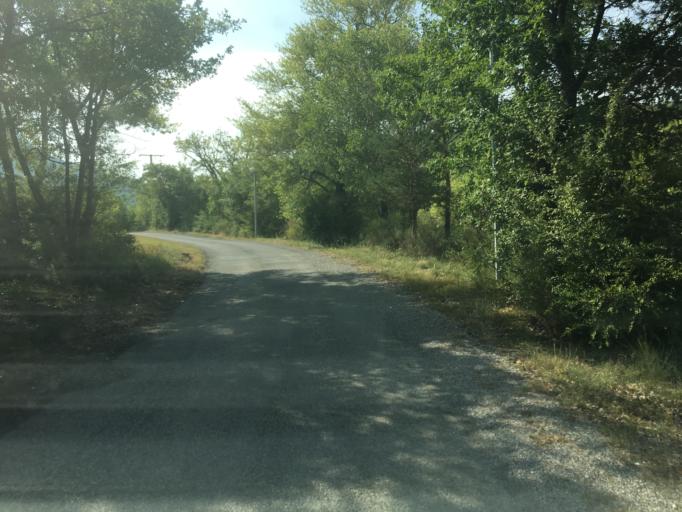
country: FR
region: Provence-Alpes-Cote d'Azur
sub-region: Departement des Alpes-de-Haute-Provence
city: Mallemoisson
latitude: 43.9389
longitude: 6.1837
